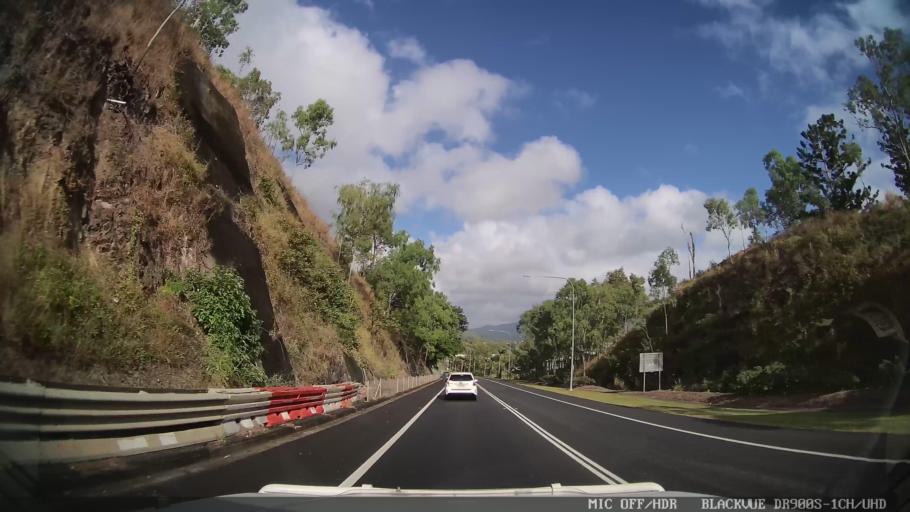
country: AU
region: Queensland
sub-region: Whitsunday
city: Proserpine
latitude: -20.2716
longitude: 148.7078
